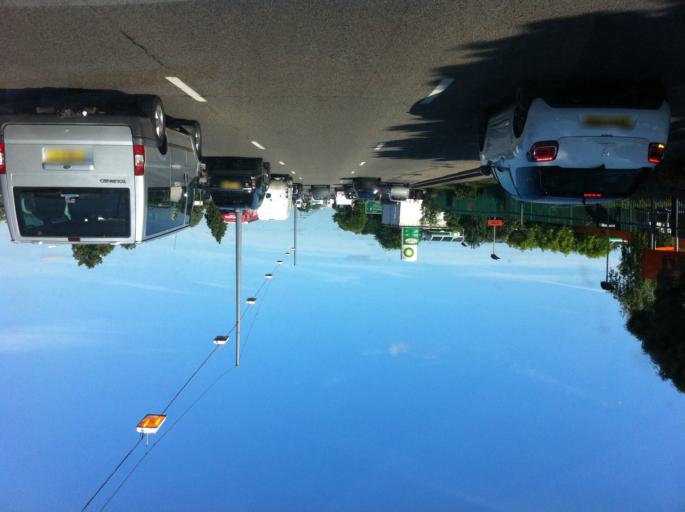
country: GB
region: England
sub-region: Greater London
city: Feltham
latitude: 51.4664
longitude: -0.4226
